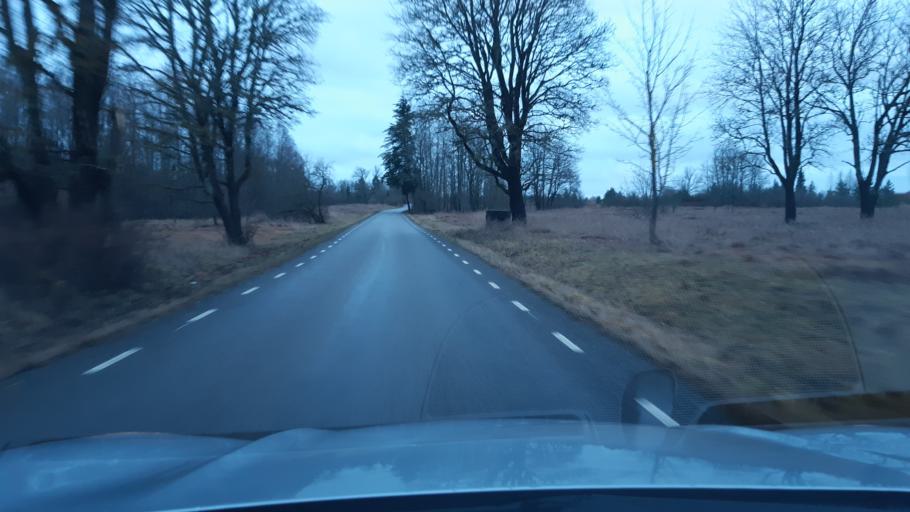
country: EE
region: Raplamaa
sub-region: Rapla vald
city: Rapla
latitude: 58.9938
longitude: 24.7222
